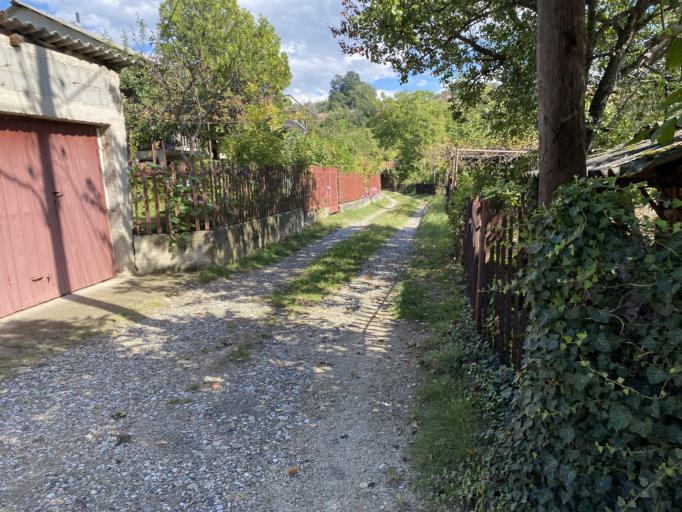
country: MK
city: Radishani
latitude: 42.0813
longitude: 21.4521
